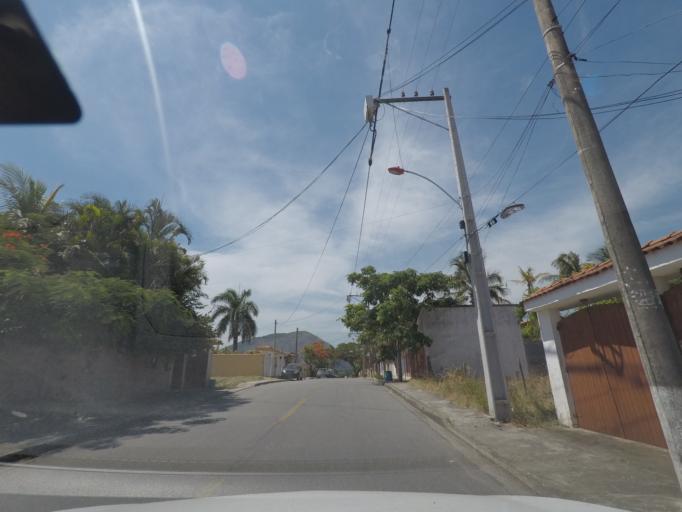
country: BR
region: Rio de Janeiro
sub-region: Marica
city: Marica
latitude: -22.9665
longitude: -42.9576
